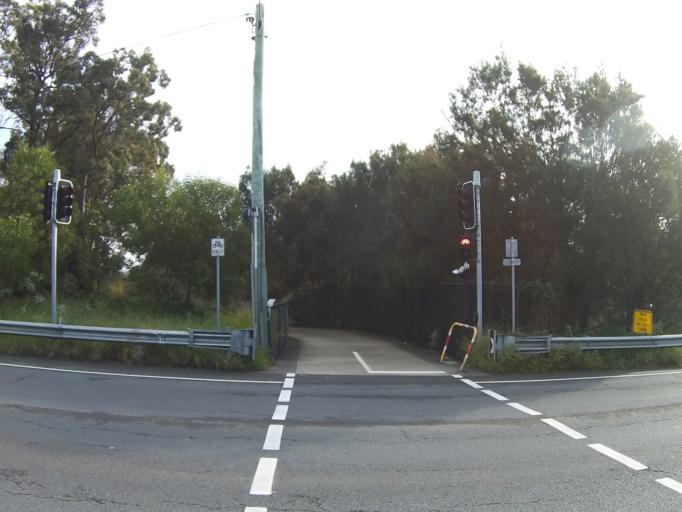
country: AU
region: Queensland
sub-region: Brisbane
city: Upper Mount Gravatt
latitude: -27.5768
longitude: 153.0997
